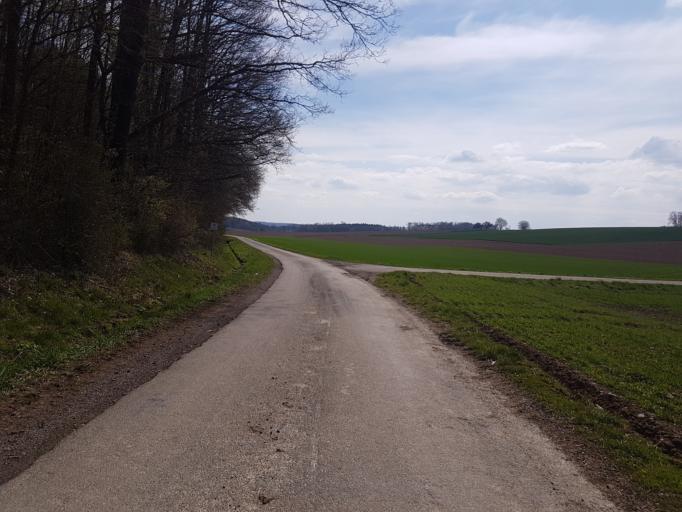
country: DE
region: Baden-Wuerttemberg
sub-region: Regierungsbezirk Stuttgart
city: Jagsthausen
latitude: 49.3769
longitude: 9.5194
